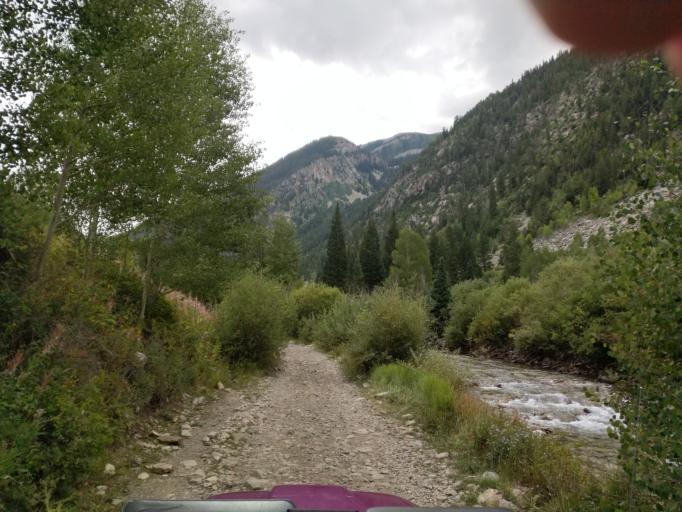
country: US
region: Colorado
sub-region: Gunnison County
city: Crested Butte
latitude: 39.0562
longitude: -107.1326
